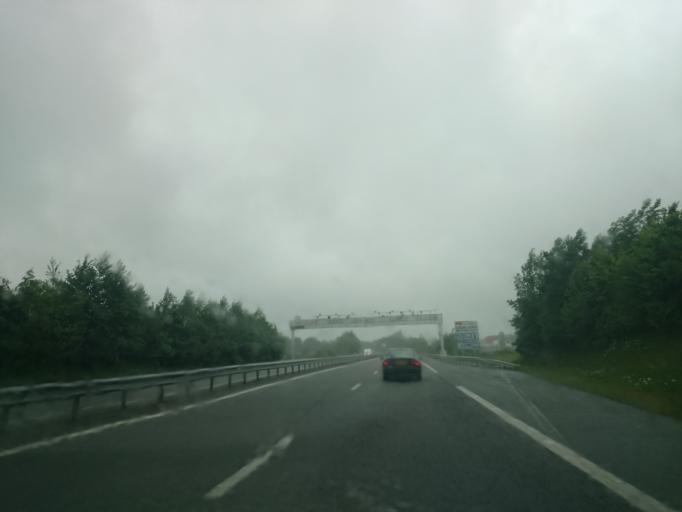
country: FR
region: Brittany
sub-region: Departement d'Ille-et-Vilaine
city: Plelan-le-Grand
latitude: 48.0078
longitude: -2.0771
